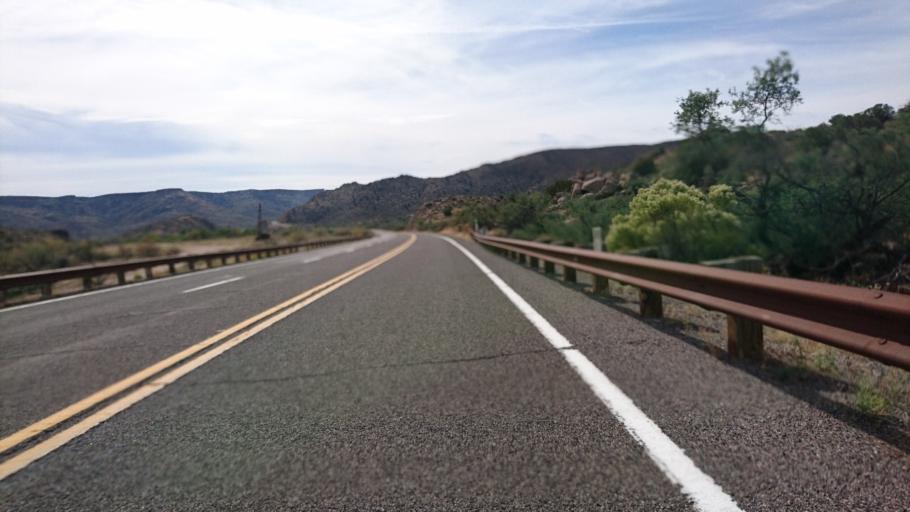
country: US
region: Arizona
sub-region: Mohave County
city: Peach Springs
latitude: 35.4317
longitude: -113.6491
